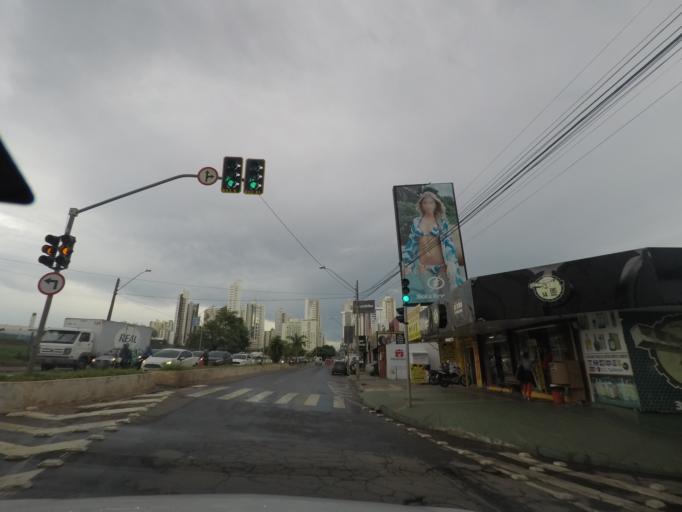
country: BR
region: Goias
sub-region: Goiania
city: Goiania
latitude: -16.7066
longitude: -49.2404
